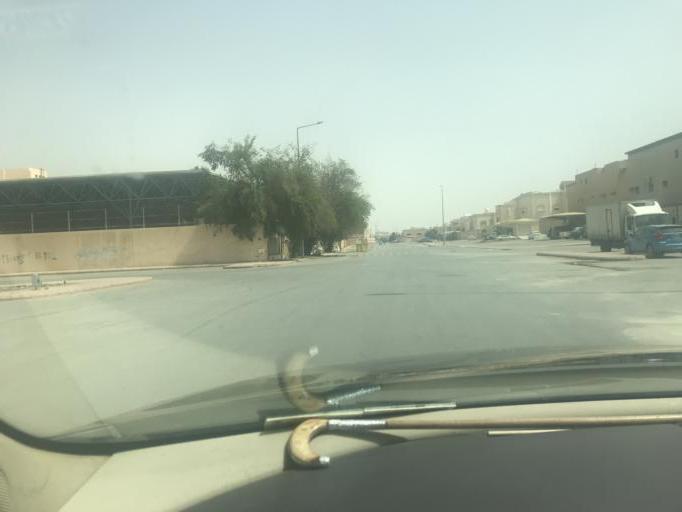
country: SA
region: Ar Riyad
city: Riyadh
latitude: 24.7436
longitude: 46.7721
